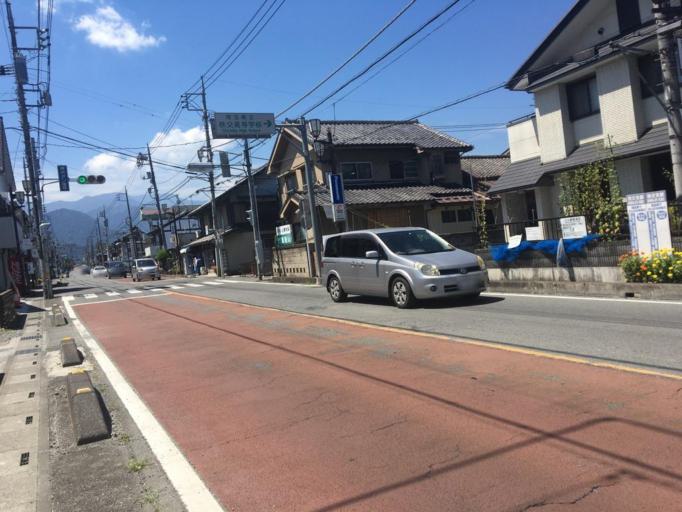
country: JP
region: Saitama
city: Chichibu
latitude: 35.9916
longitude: 139.0795
